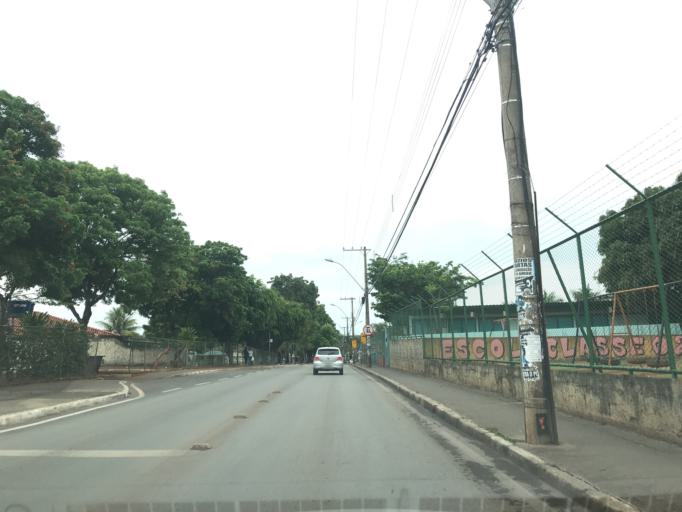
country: BR
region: Federal District
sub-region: Brasilia
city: Brasilia
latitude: -15.8518
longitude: -47.9512
